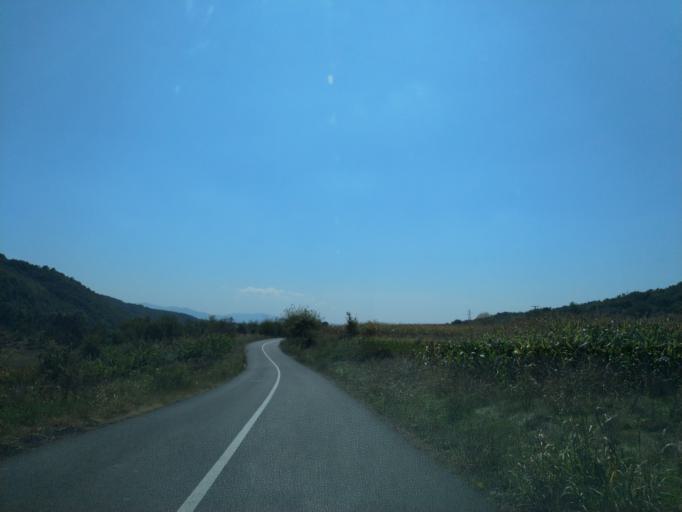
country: RS
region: Central Serbia
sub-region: Rasinski Okrug
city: Krusevac
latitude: 43.6376
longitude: 21.3746
